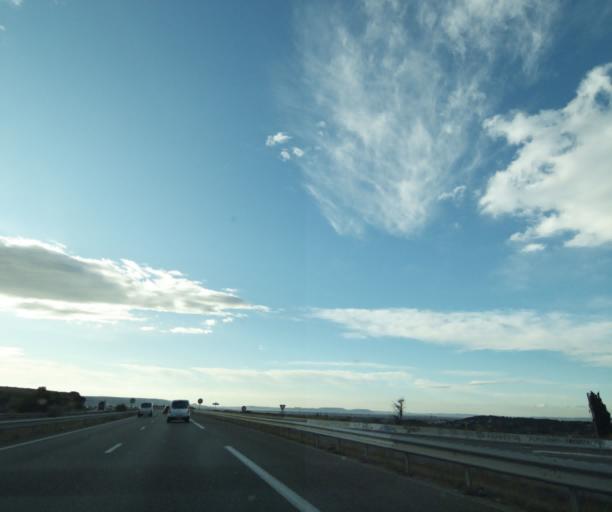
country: FR
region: Provence-Alpes-Cote d'Azur
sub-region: Departement des Bouches-du-Rhone
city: Gignac-la-Nerthe
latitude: 43.3919
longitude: 5.2555
